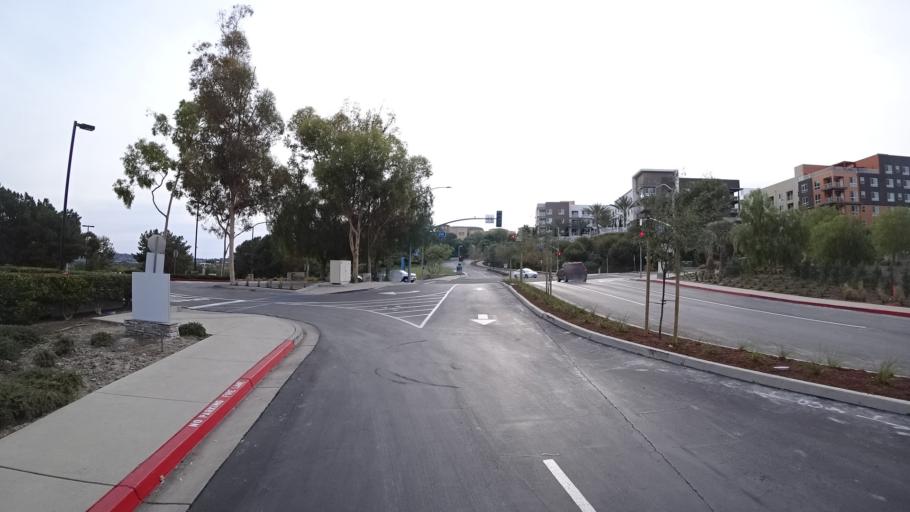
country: US
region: California
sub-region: Orange County
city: Aliso Viejo
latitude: 33.5811
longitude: -117.7261
